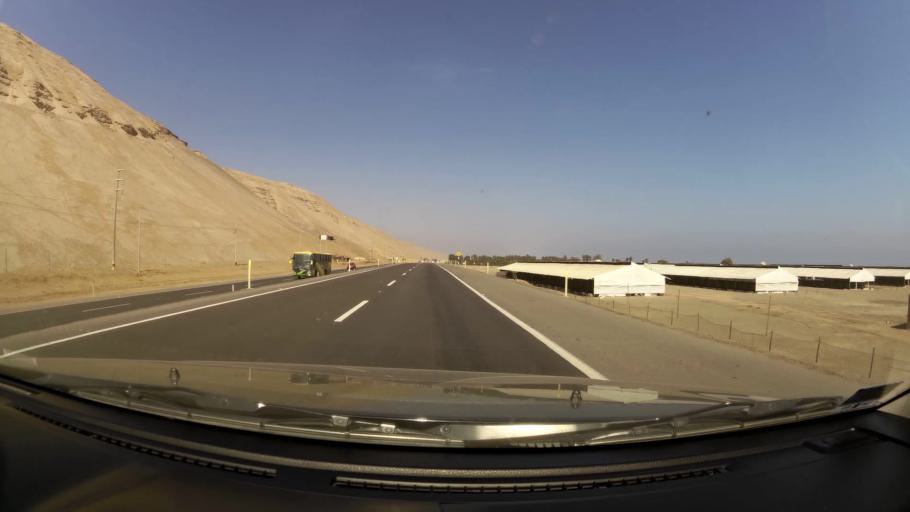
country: PE
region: Ica
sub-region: Provincia de Chincha
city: San Pedro
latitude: -13.3581
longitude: -76.2187
